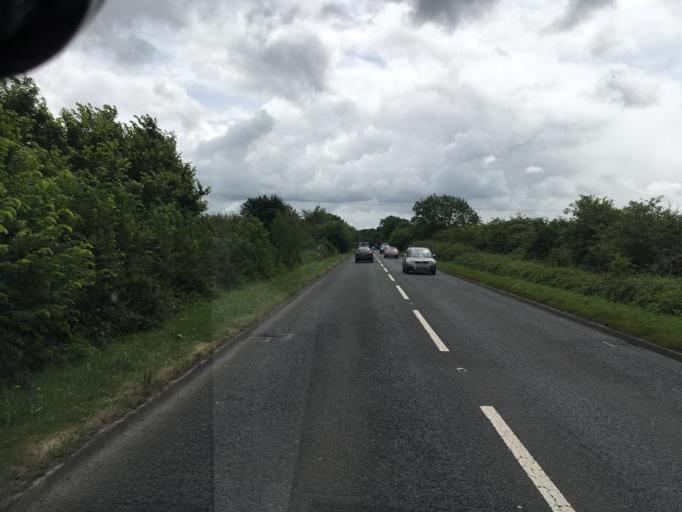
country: GB
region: England
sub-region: Gloucestershire
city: Stonehouse
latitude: 51.7569
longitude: -2.3180
